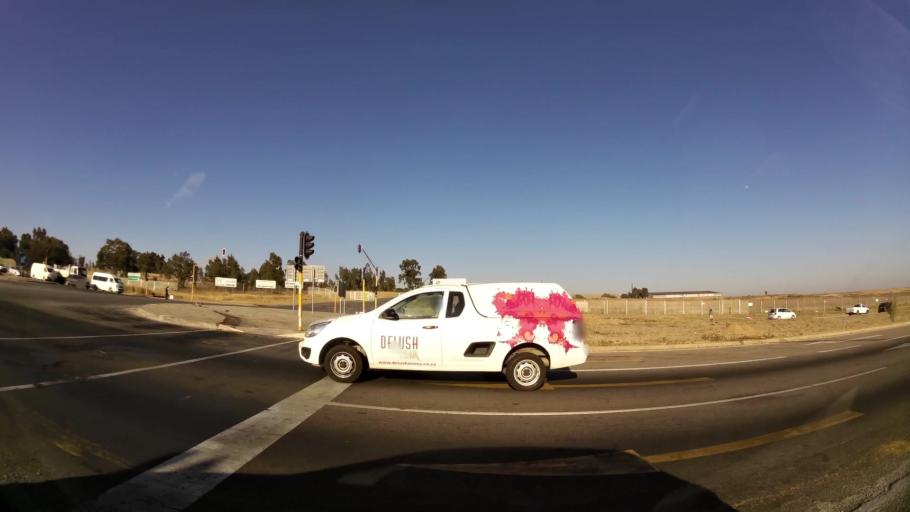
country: ZA
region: Gauteng
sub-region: City of Johannesburg Metropolitan Municipality
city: Modderfontein
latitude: -26.0496
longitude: 28.1578
